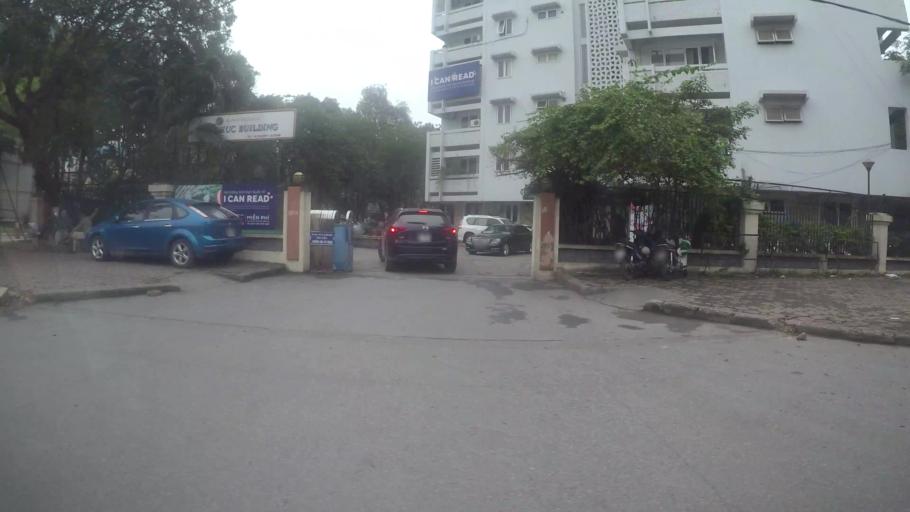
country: VN
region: Ha Noi
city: Dong Da
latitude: 21.0319
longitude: 105.8213
